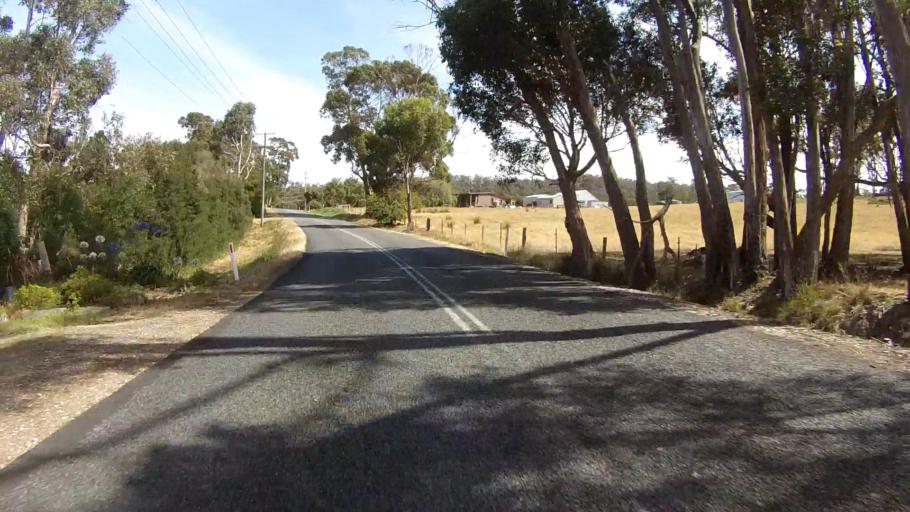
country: AU
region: Tasmania
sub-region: Huon Valley
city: Cygnet
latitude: -43.2757
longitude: 147.1620
